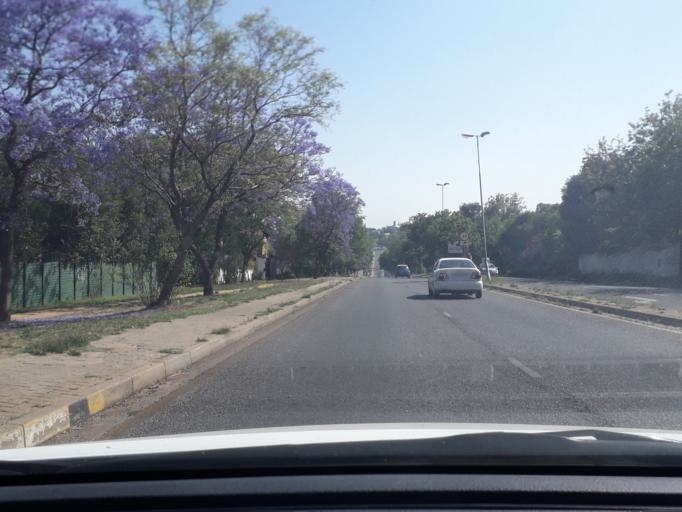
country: ZA
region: Gauteng
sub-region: City of Johannesburg Metropolitan Municipality
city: Roodepoort
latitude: -26.1108
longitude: 27.9731
